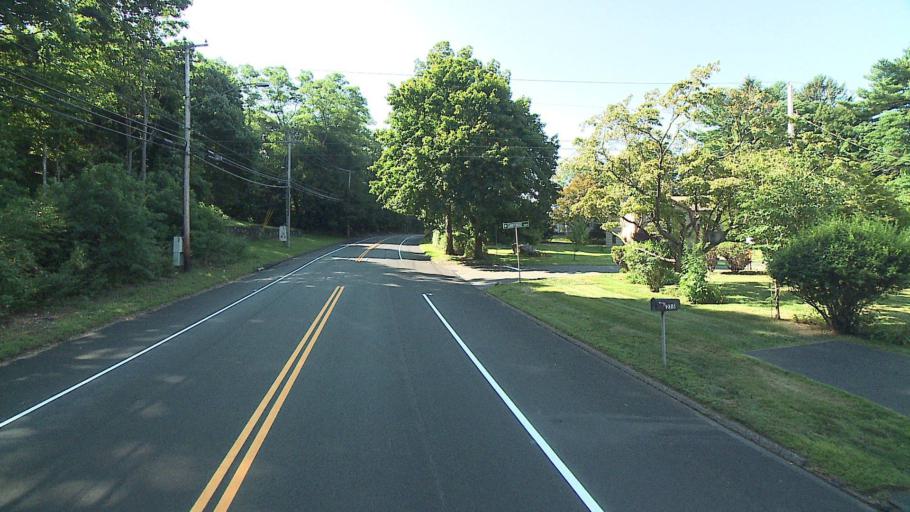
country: US
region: Connecticut
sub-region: Fairfield County
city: Trumbull
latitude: 41.2318
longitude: -73.1773
